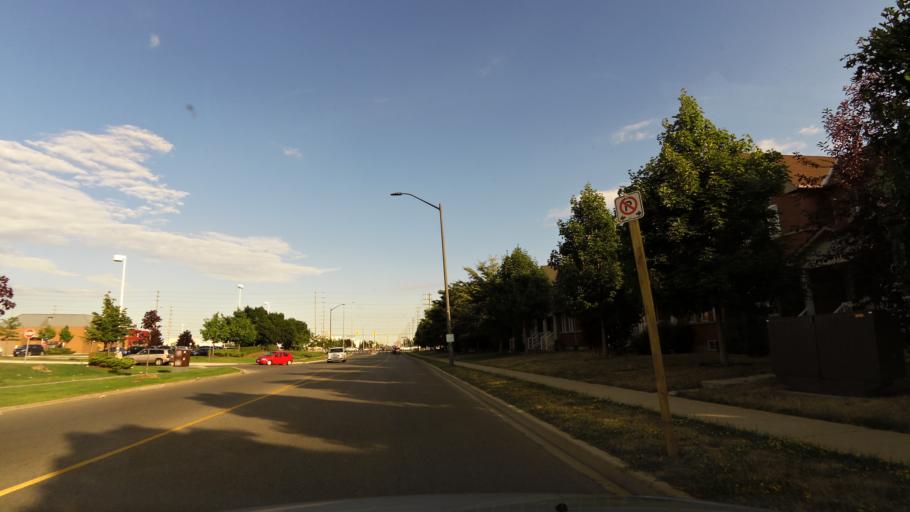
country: CA
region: Ontario
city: Mississauga
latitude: 43.6084
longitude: -79.7026
